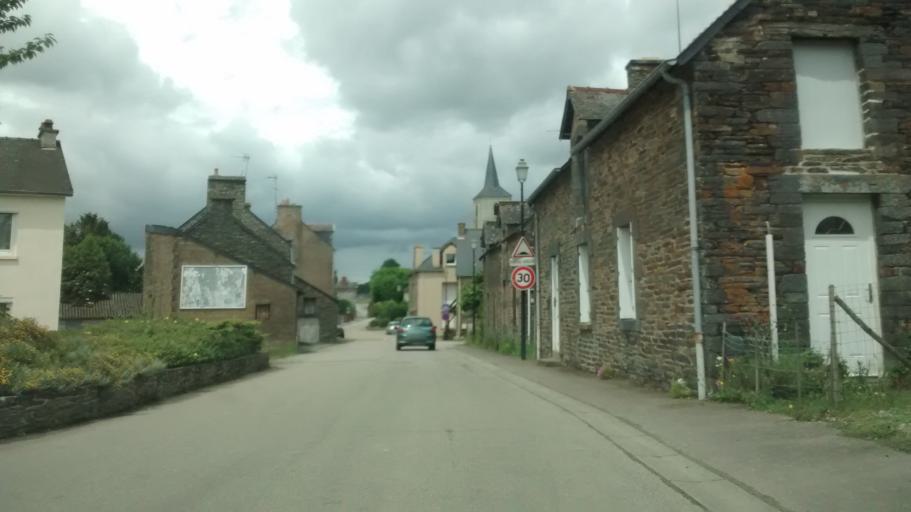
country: FR
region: Brittany
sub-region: Departement d'Ille-et-Vilaine
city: Sixt-sur-Aff
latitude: 47.7833
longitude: -2.1060
